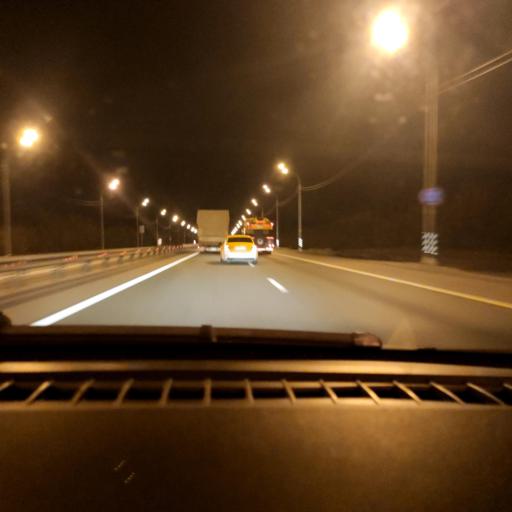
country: RU
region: Lipetsk
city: Khlevnoye
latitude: 52.2333
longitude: 39.0849
